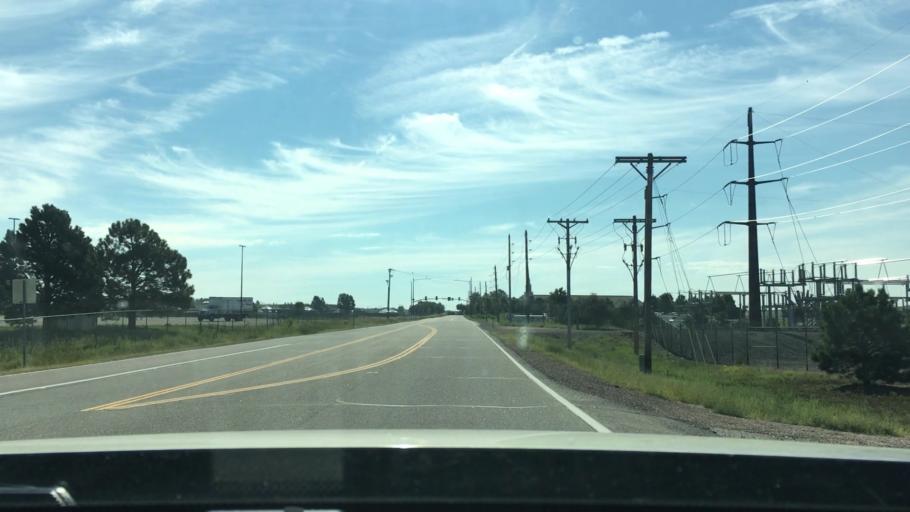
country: US
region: Colorado
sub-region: Douglas County
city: The Pinery
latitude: 39.4343
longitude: -104.7571
